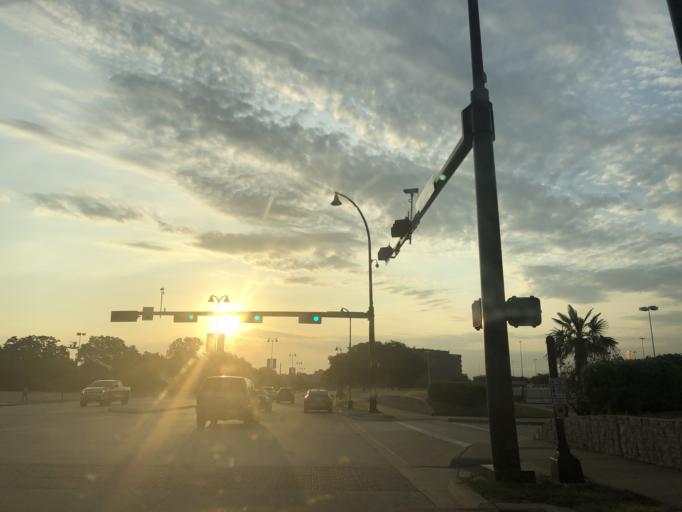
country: US
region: Texas
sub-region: Tarrant County
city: Arlington
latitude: 32.7628
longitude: -97.0817
